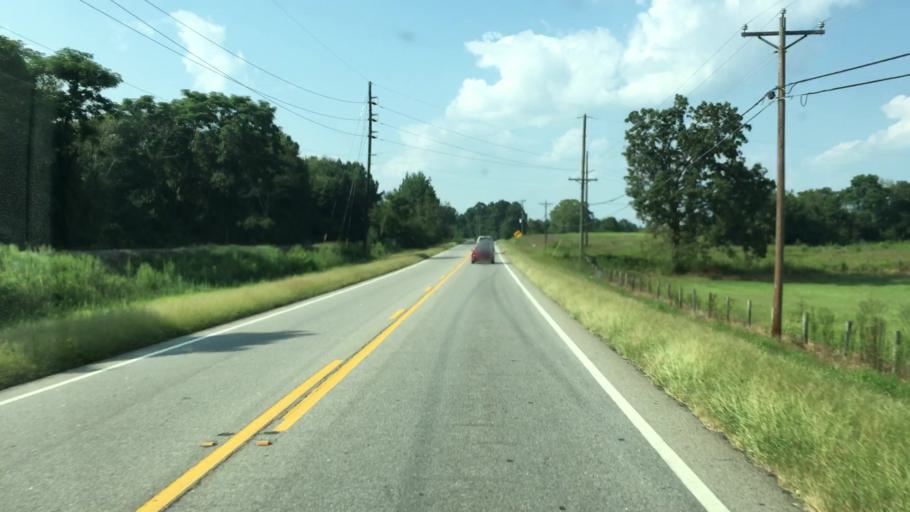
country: US
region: Georgia
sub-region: Walton County
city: Social Circle
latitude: 33.7017
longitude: -83.7021
